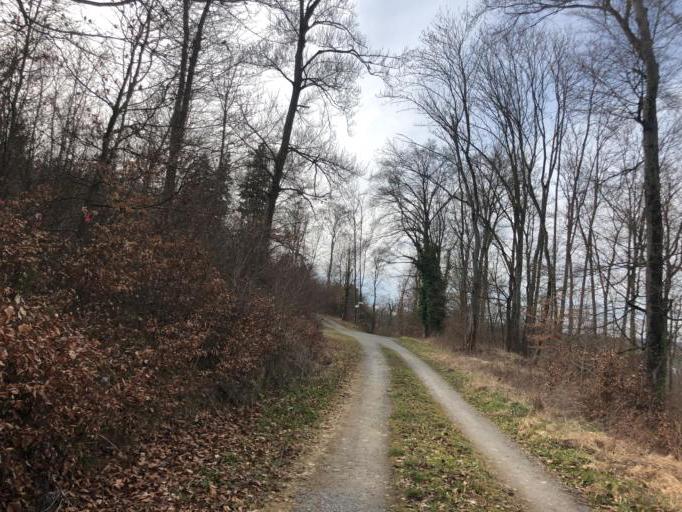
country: DE
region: Baden-Wuerttemberg
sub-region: Karlsruhe Region
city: Muhlacker
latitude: 48.9253
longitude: 8.8820
